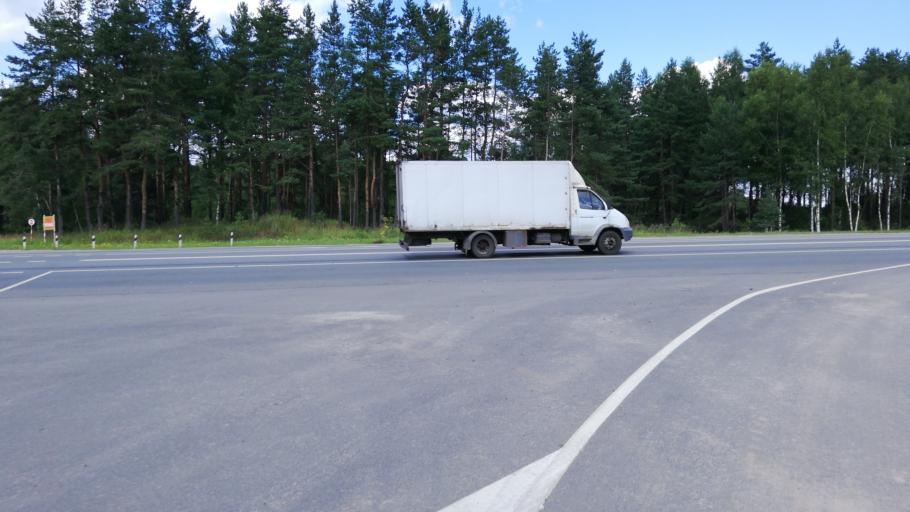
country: RU
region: Jaroslavl
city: Levashevo
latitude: 57.6389
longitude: 40.4612
